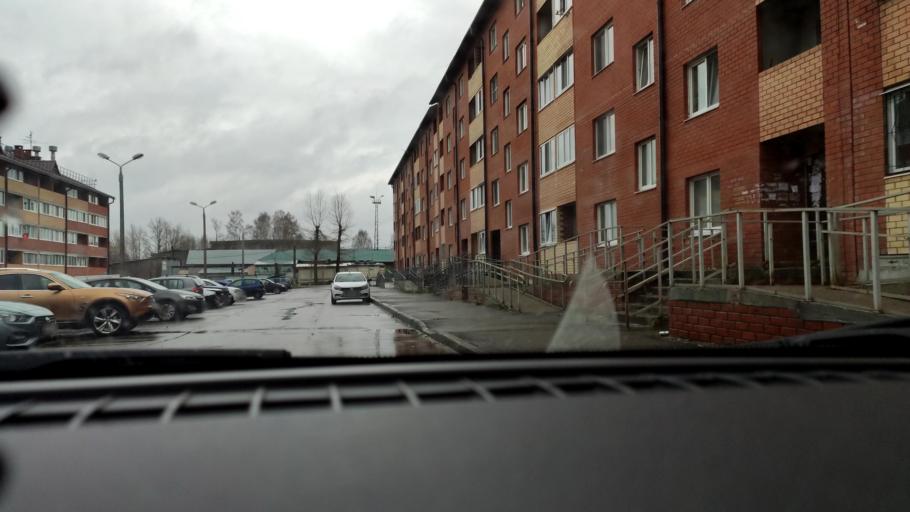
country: RU
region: Perm
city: Perm
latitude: 58.0958
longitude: 56.3691
